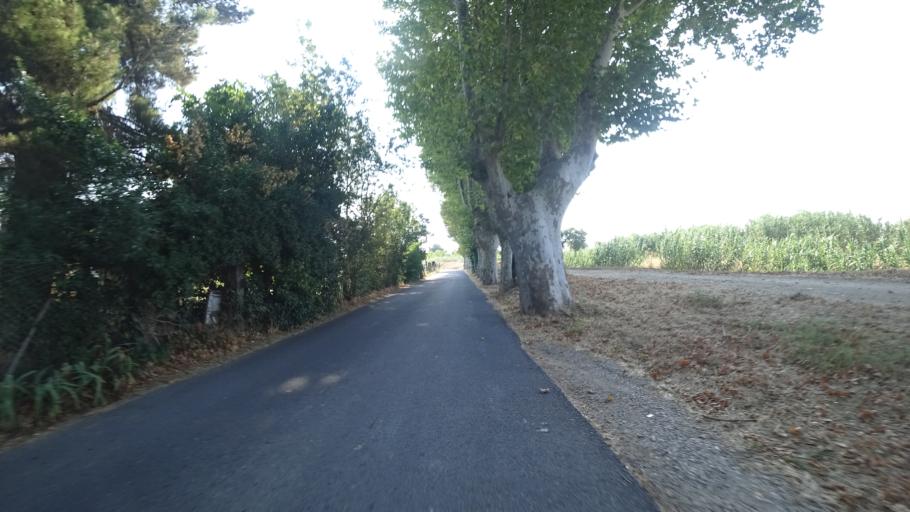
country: FR
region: Languedoc-Roussillon
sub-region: Departement des Pyrenees-Orientales
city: Claira
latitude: 42.7587
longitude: 2.9700
